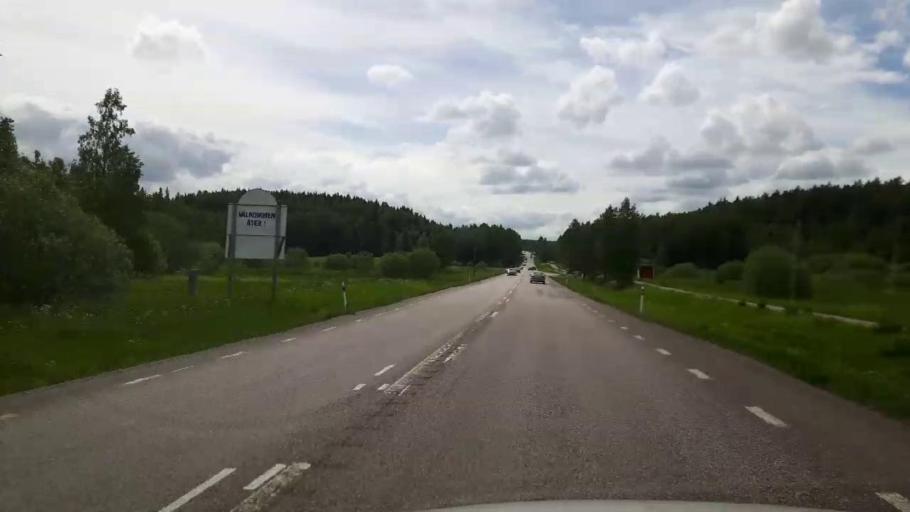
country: SE
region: Vaestmanland
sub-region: Fagersta Kommun
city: Fagersta
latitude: 59.9731
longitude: 15.7818
